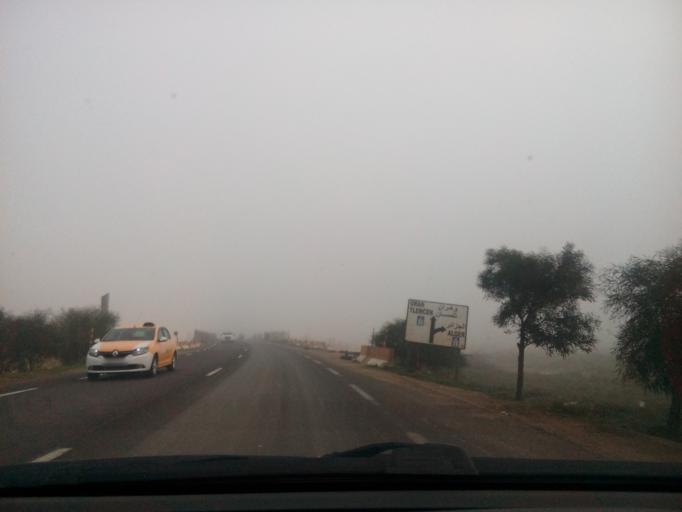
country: DZ
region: Relizane
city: Relizane
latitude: 35.7900
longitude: 0.5339
